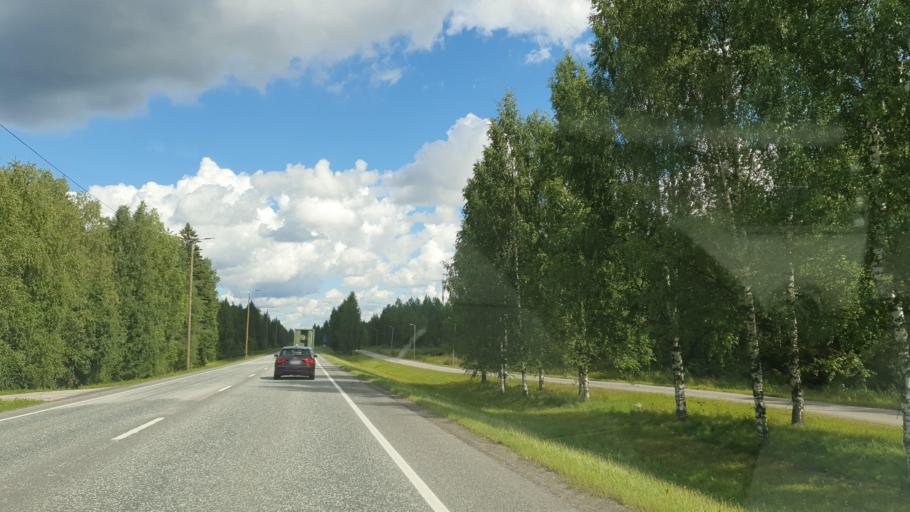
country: FI
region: Kainuu
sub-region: Kajaani
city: Kajaani
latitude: 64.2043
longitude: 27.6450
